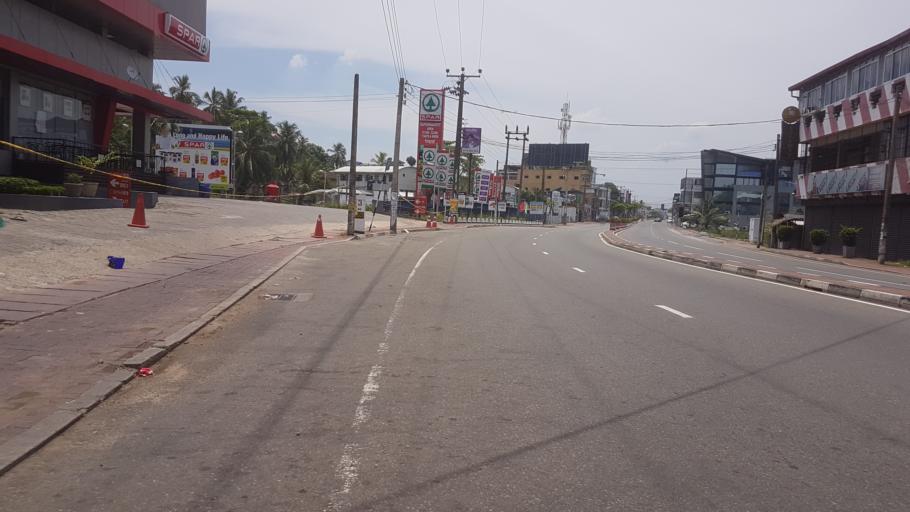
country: LK
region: Western
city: Battaramulla South
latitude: 6.8824
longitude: 79.9338
